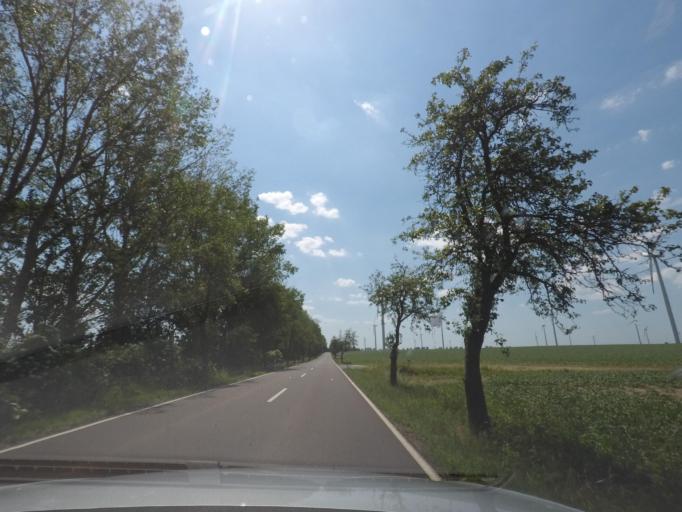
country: DE
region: Saxony-Anhalt
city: Eichenbarleben
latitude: 52.2034
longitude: 11.3873
